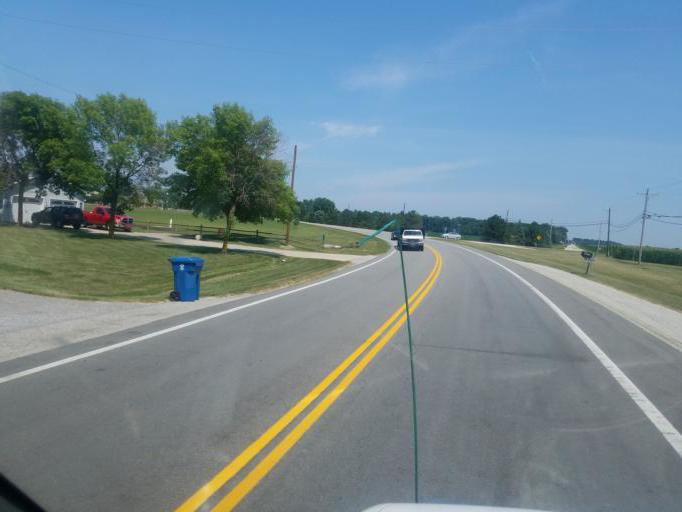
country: US
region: Ohio
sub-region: Auglaize County
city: Saint Marys
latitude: 40.5096
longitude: -84.4303
